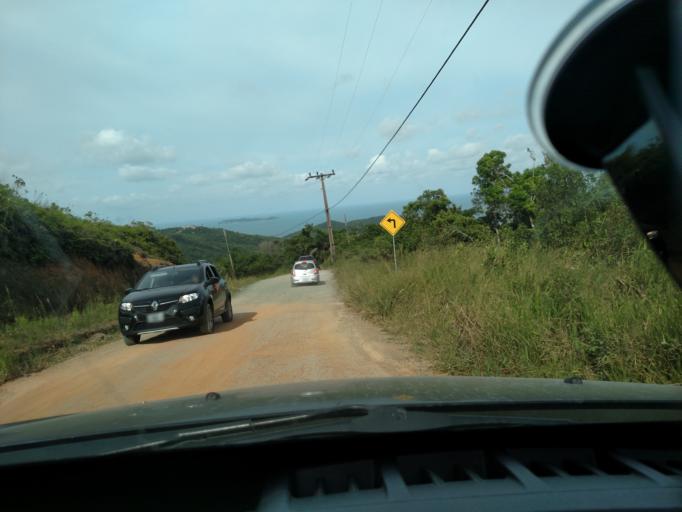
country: BR
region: Santa Catarina
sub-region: Porto Belo
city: Porto Belo
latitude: -27.2106
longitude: -48.4983
